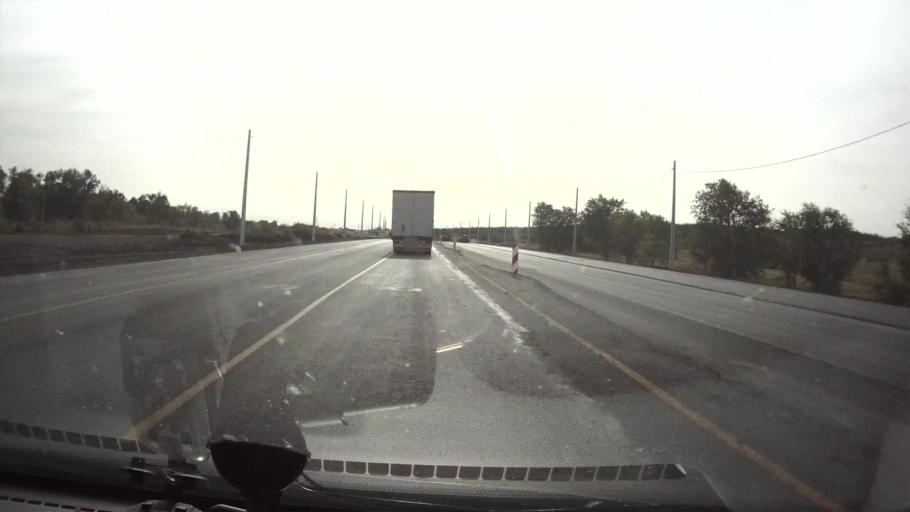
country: RU
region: Saratov
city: Sinodskoye
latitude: 52.0190
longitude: 46.7023
